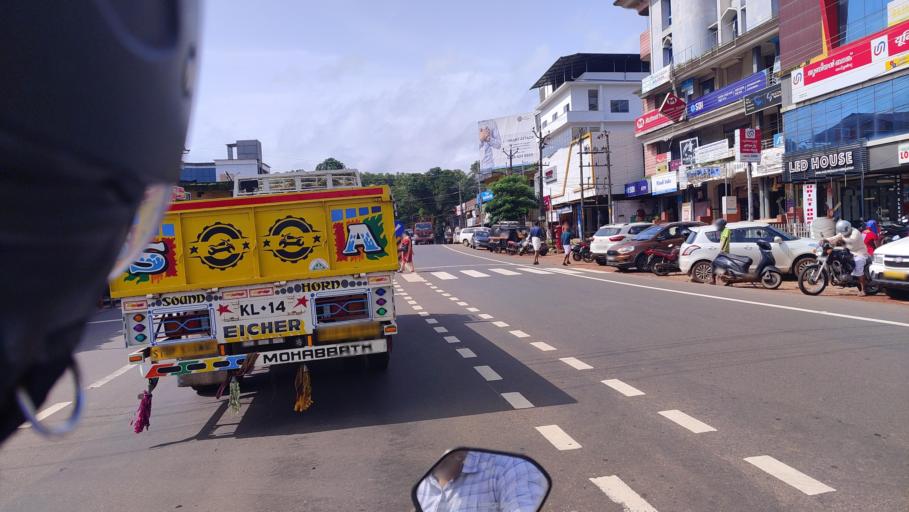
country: IN
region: Kerala
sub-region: Kasaragod District
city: Nileshwar
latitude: 12.2165
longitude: 75.1625
